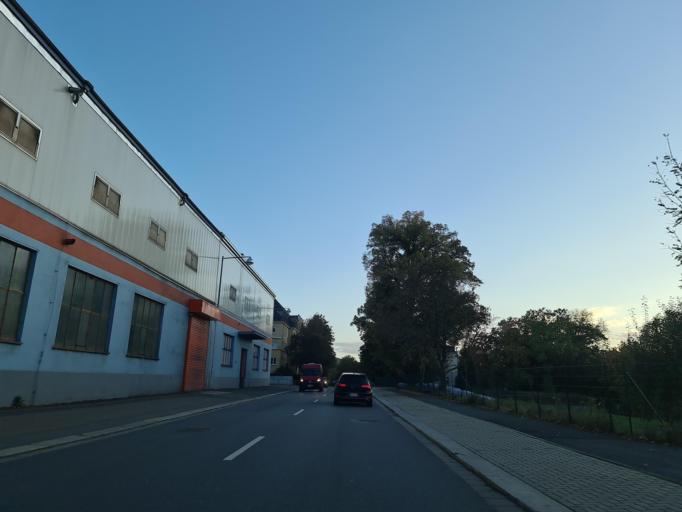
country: DE
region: Saxony
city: Elsterberg
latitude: 50.6156
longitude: 12.1697
